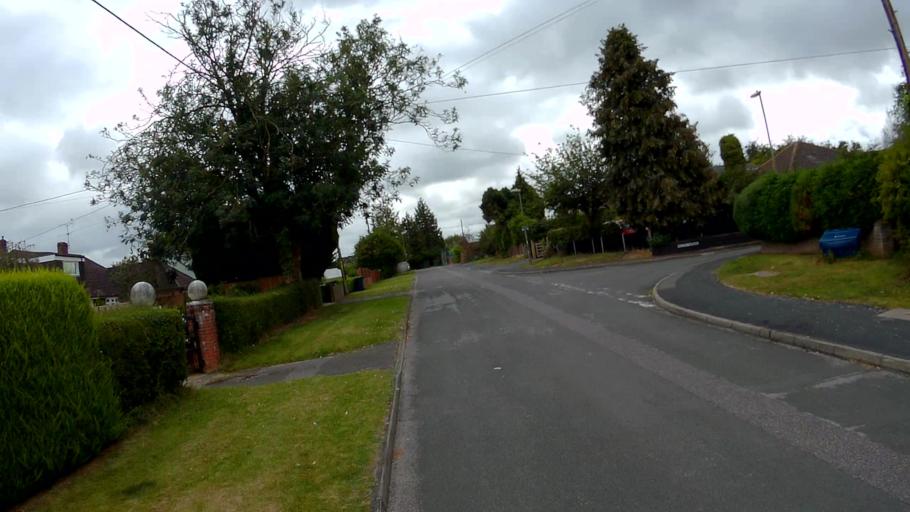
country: GB
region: England
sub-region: Hampshire
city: Basingstoke
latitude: 51.2538
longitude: -1.1383
